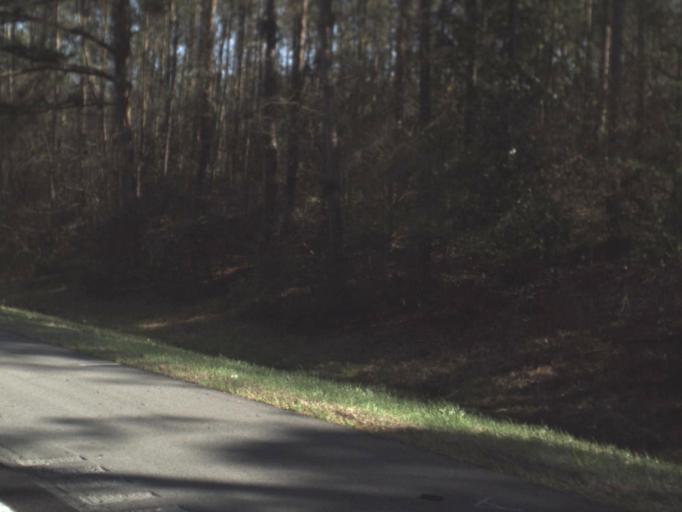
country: US
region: Florida
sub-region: Jackson County
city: Sneads
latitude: 30.6283
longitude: -84.8902
